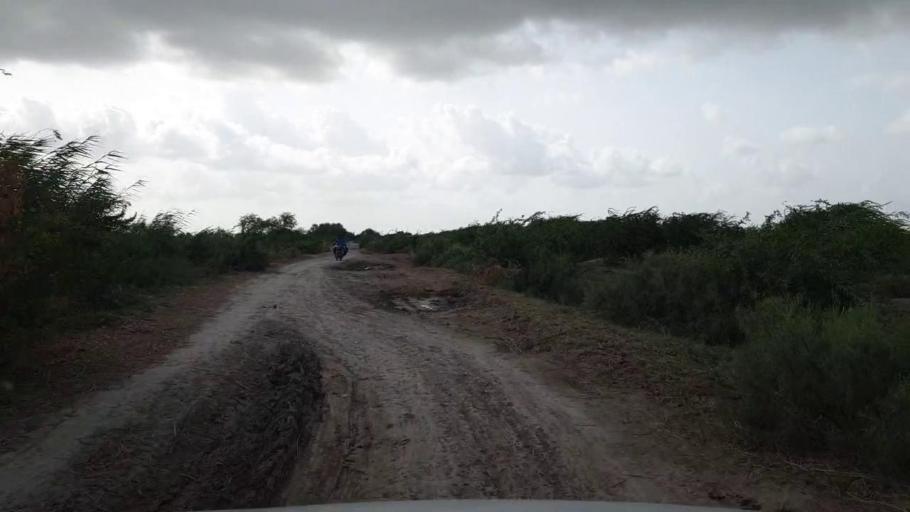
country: PK
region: Sindh
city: Kario
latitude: 24.7492
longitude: 68.6164
